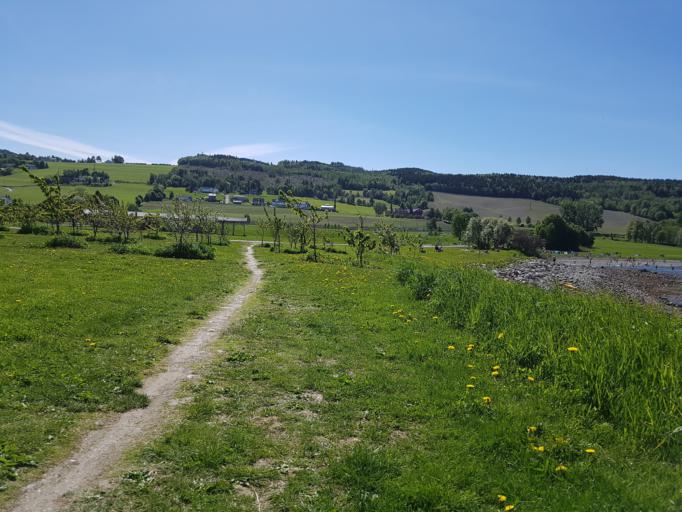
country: NO
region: Sor-Trondelag
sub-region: Malvik
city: Malvik
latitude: 63.4350
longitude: 10.7264
